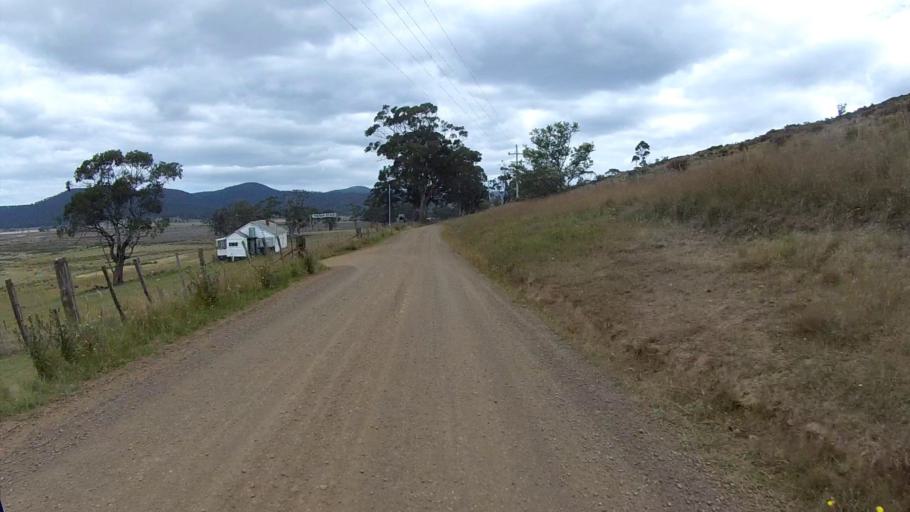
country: AU
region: Tasmania
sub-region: Sorell
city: Sorell
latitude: -42.6301
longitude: 147.9287
